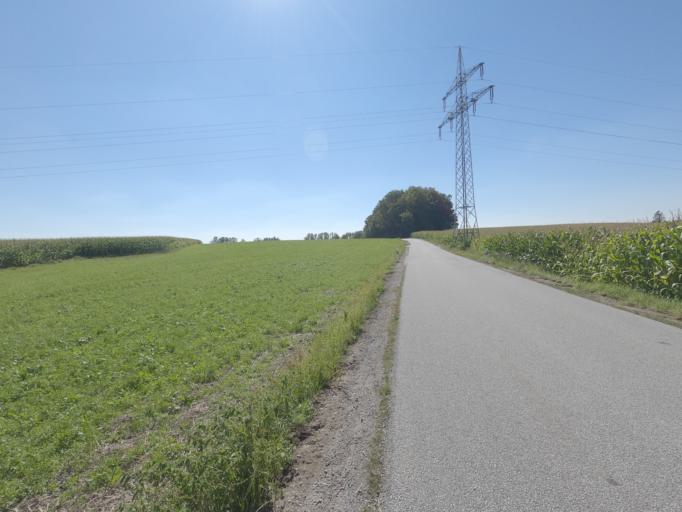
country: DE
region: Bavaria
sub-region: Lower Bavaria
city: Deggendorf
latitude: 48.8277
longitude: 13.0010
